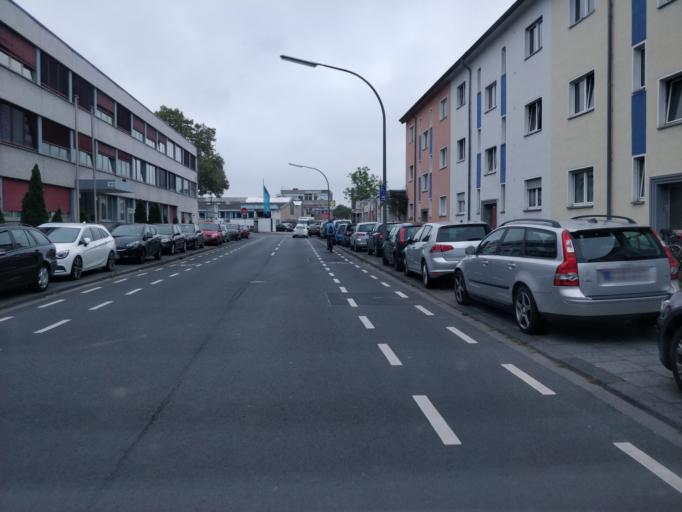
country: DE
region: North Rhine-Westphalia
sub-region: Regierungsbezirk Koln
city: Mengenich
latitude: 50.9461
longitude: 6.8898
